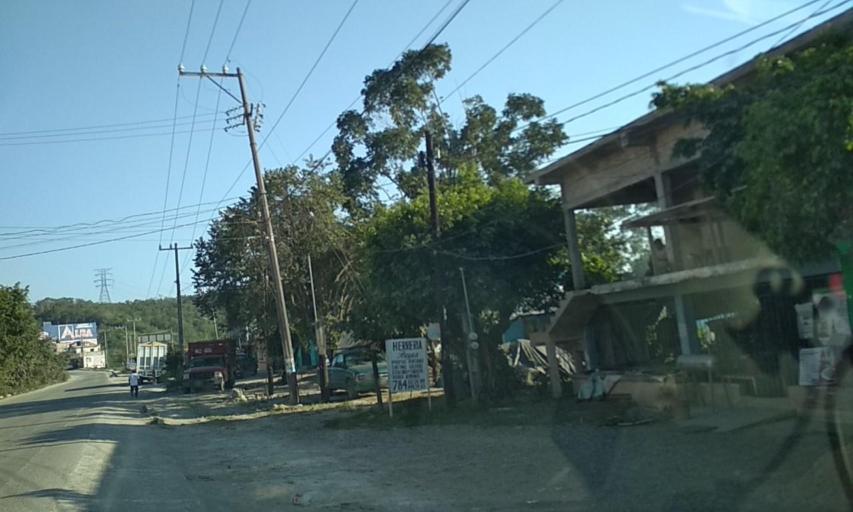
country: MX
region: Veracruz
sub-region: Papantla
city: El Chote
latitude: 20.4042
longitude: -97.3423
